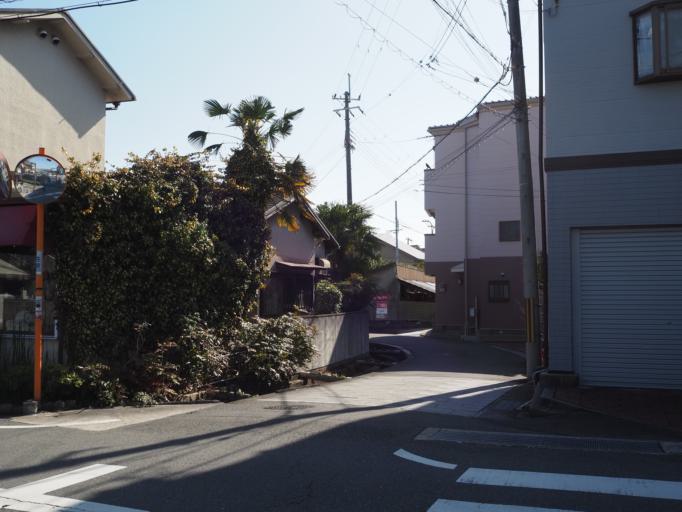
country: JP
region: Hyogo
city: Itami
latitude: 34.7927
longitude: 135.4171
